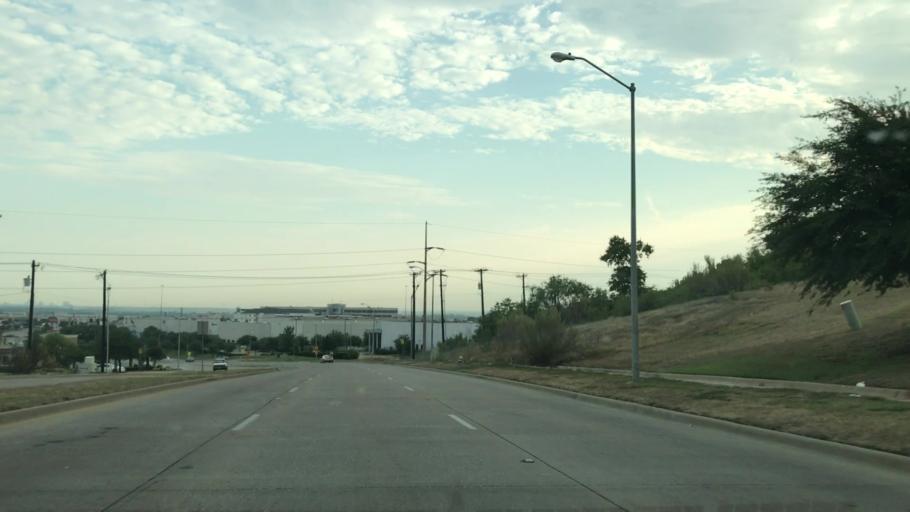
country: US
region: Texas
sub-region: Dallas County
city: Cockrell Hill
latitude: 32.7578
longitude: -96.8929
